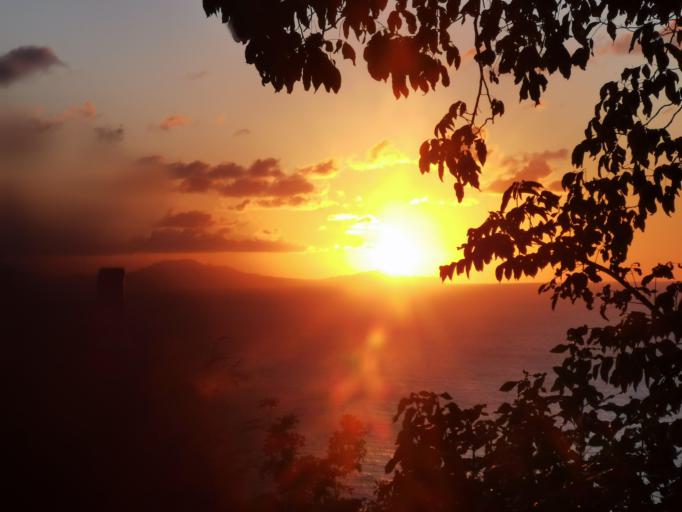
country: AG
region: Saint Paul
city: Falmouth
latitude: 17.0025
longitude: -61.7549
